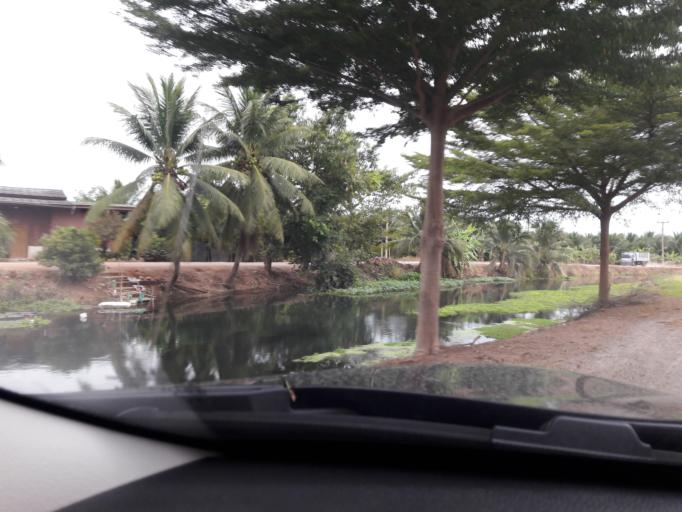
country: TH
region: Ratchaburi
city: Bang Phae
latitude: 13.6185
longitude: 99.9625
